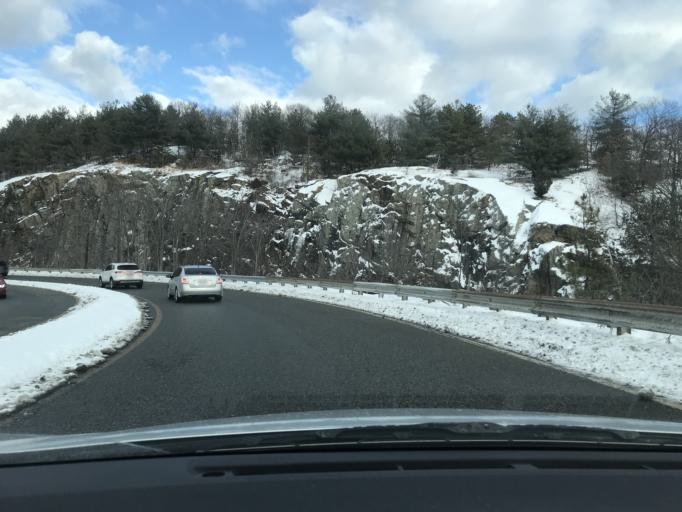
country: US
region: Massachusetts
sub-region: Essex County
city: Saugus
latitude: 42.4801
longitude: -71.0197
